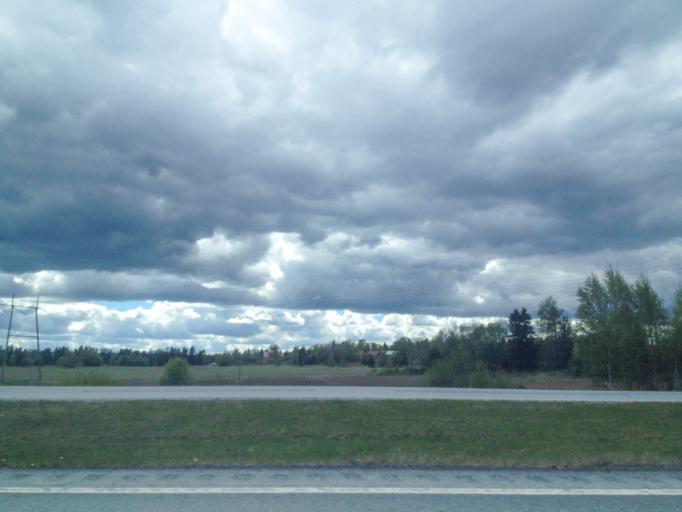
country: FI
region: Pirkanmaa
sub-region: Etelae-Pirkanmaa
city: Akaa
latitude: 61.1687
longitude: 23.9405
